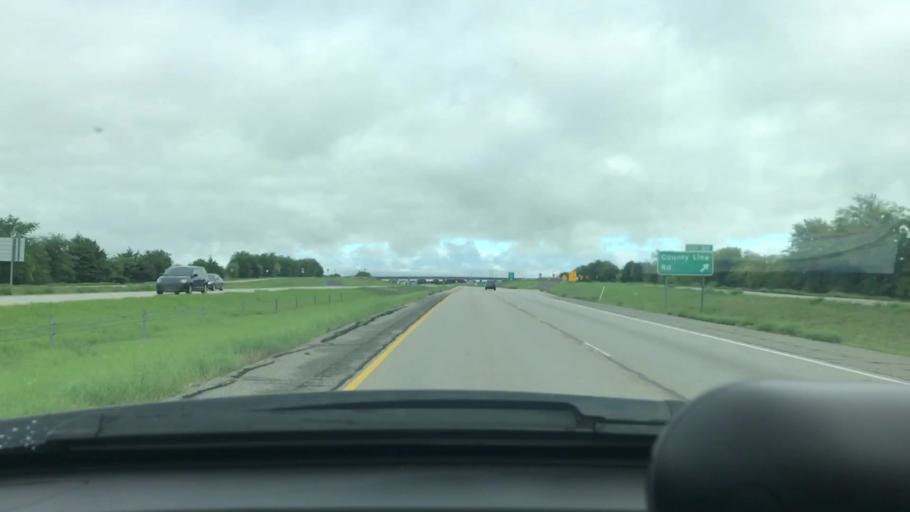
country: US
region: Texas
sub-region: Grayson County
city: Van Alstyne
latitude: 33.3954
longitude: -96.5803
